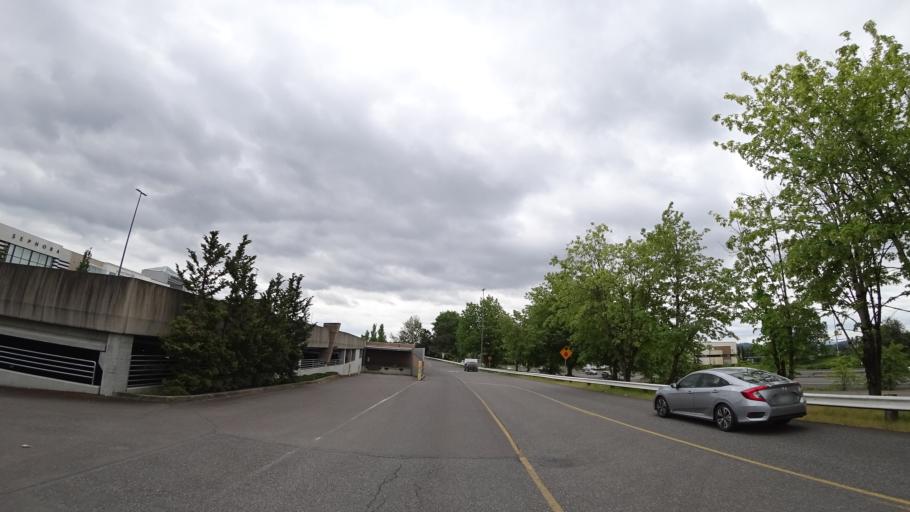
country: US
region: Oregon
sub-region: Washington County
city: Tigard
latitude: 45.4511
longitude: -122.7834
